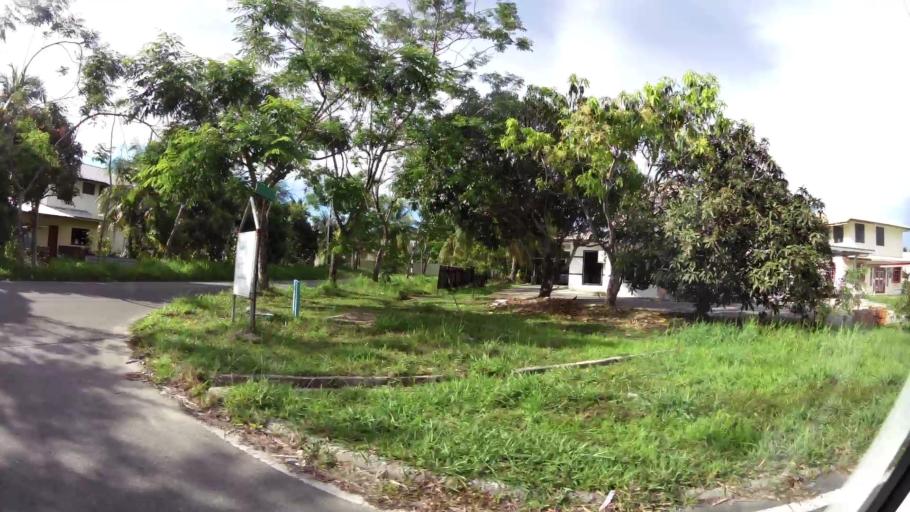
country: BN
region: Brunei and Muara
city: Bandar Seri Begawan
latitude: 4.9718
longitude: 115.0259
